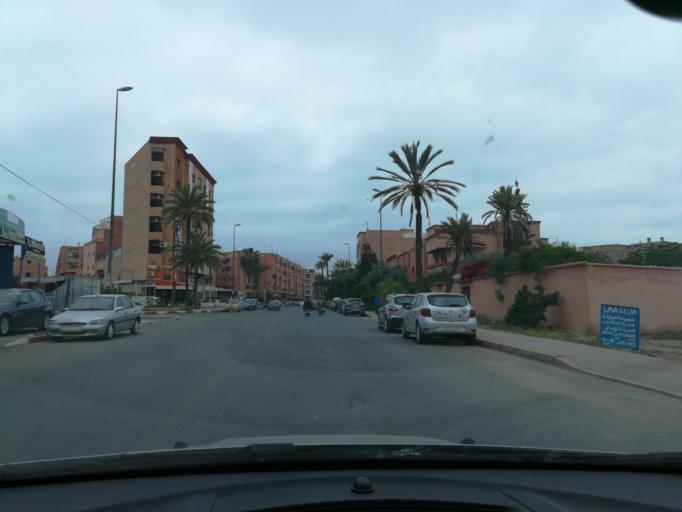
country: MA
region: Marrakech-Tensift-Al Haouz
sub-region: Marrakech
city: Marrakesh
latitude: 31.6490
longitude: -8.0064
